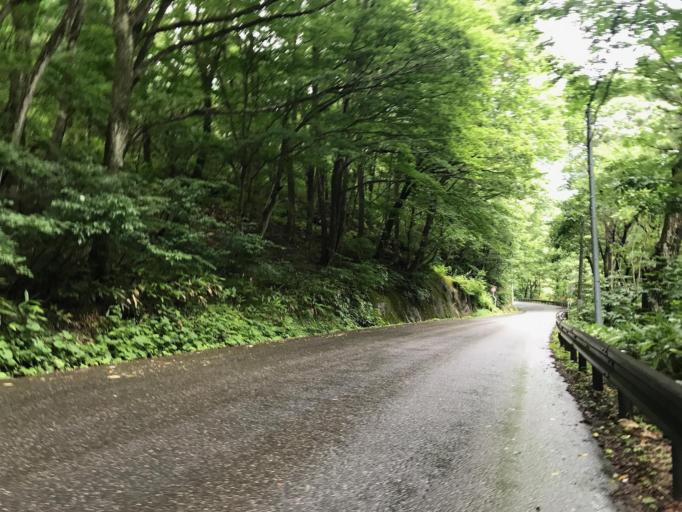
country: JP
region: Gunma
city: Numata
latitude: 36.8188
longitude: 138.9816
